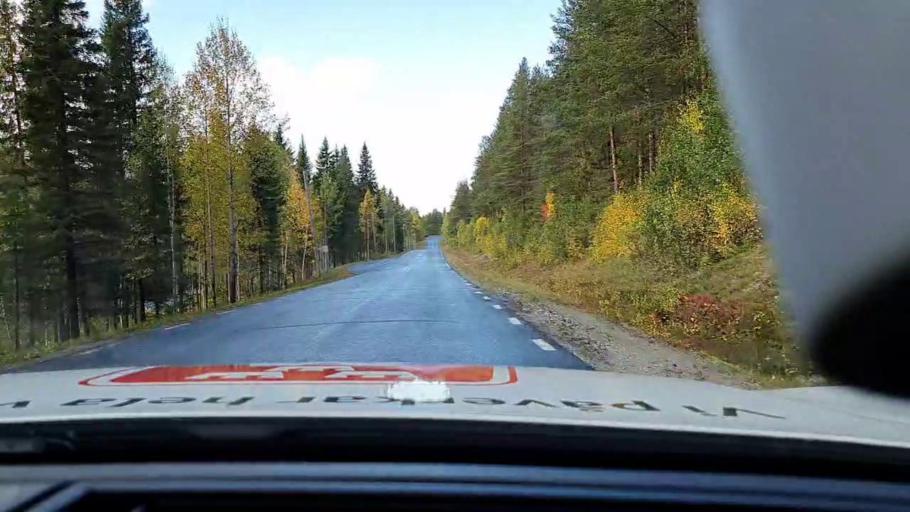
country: SE
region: Vaesterbotten
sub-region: Skelleftea Kommun
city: Langsele
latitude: 64.9449
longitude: 20.0319
